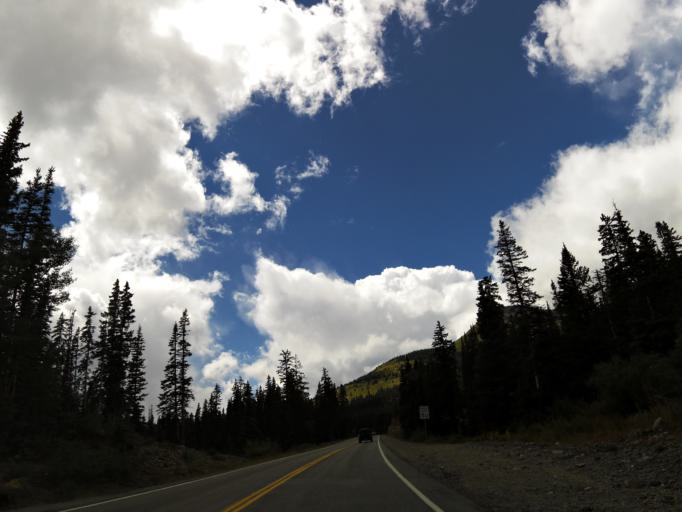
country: US
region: Colorado
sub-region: San Juan County
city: Silverton
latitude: 37.7672
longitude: -107.6737
